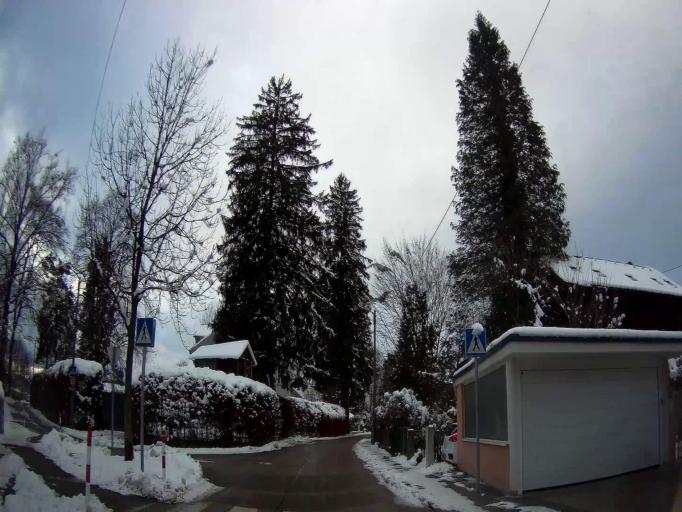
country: AT
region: Salzburg
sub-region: Salzburg Stadt
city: Salzburg
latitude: 47.7895
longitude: 13.0809
